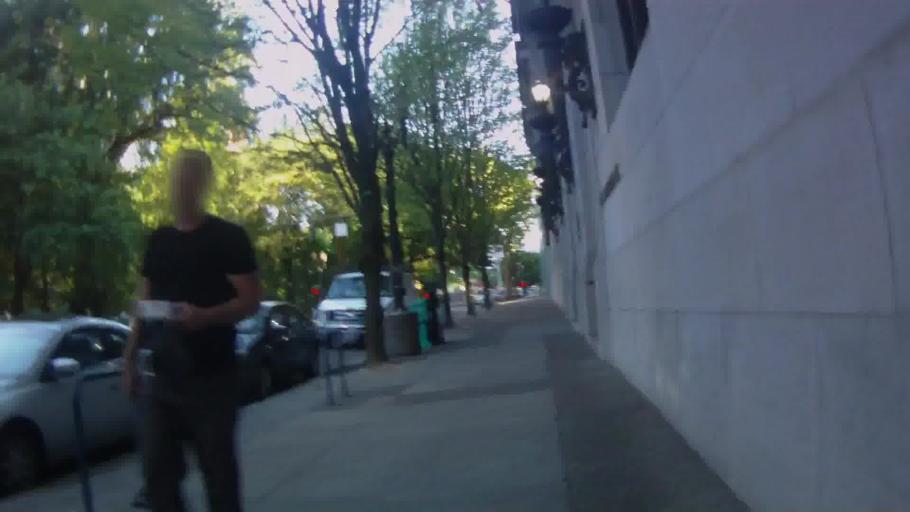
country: US
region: Oregon
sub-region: Multnomah County
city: Portland
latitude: 45.5164
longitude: -122.6778
